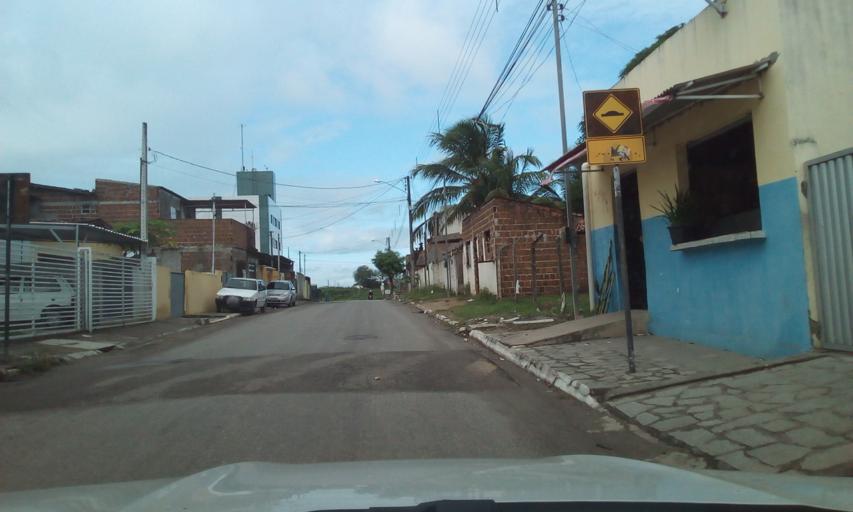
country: BR
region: Paraiba
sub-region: Conde
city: Conde
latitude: -7.2125
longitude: -34.8496
